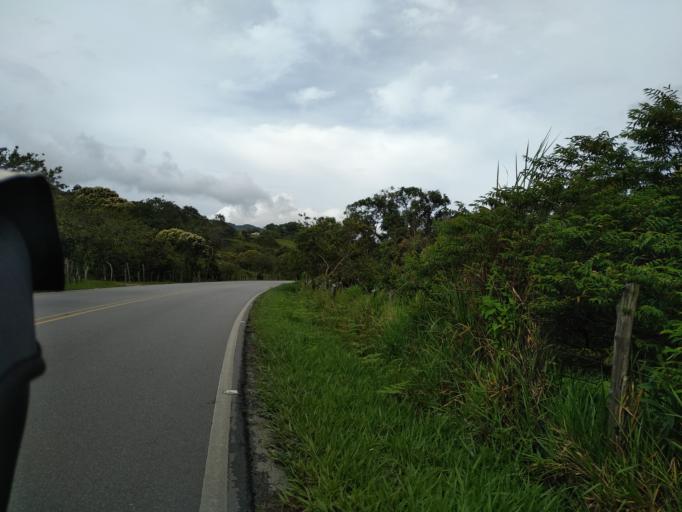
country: CO
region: Santander
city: Suaita
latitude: 6.1082
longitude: -73.3668
